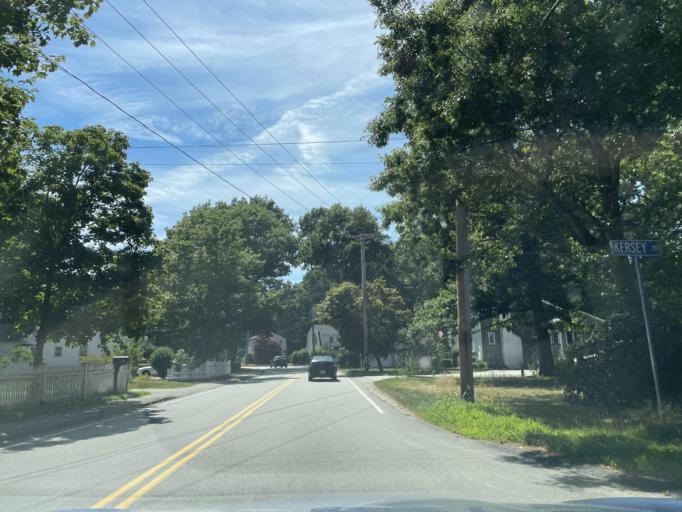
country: US
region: Massachusetts
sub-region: Norfolk County
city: Foxborough
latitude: 42.0761
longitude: -71.2488
